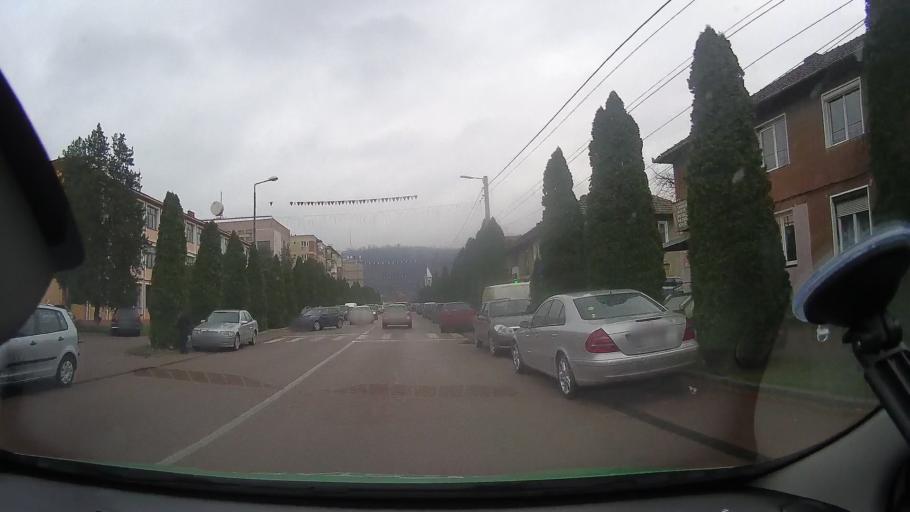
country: RO
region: Arad
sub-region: Comuna Sebis
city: Sebis
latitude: 46.3714
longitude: 22.1284
